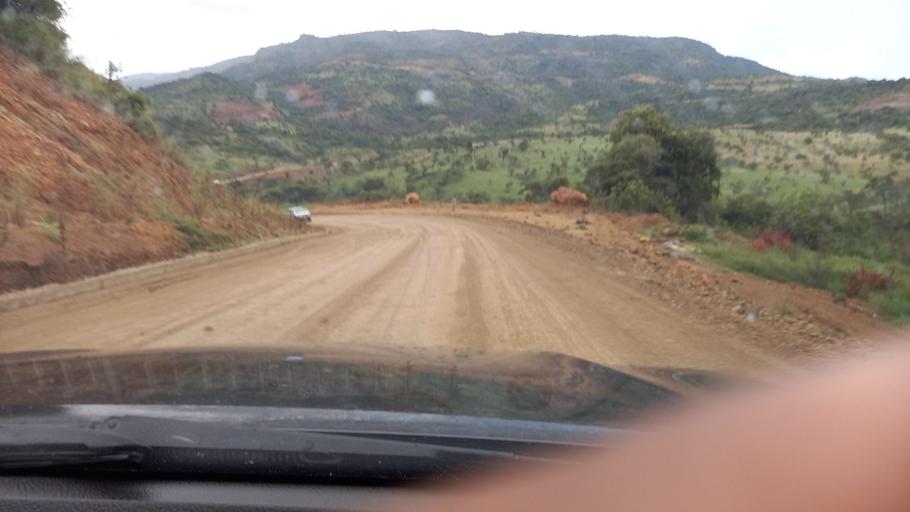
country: ET
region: Southern Nations, Nationalities, and People's Region
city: Mizan Teferi
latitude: 6.1910
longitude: 35.6798
